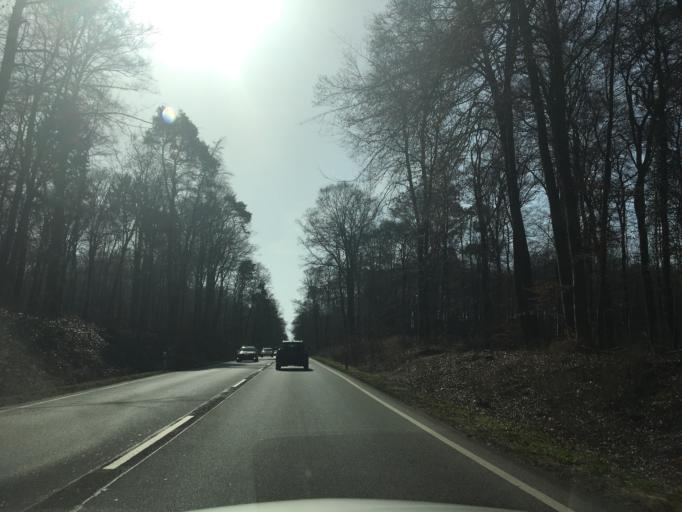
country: DE
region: Hesse
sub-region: Regierungsbezirk Darmstadt
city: Neu Isenburg
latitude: 50.0742
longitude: 8.6932
